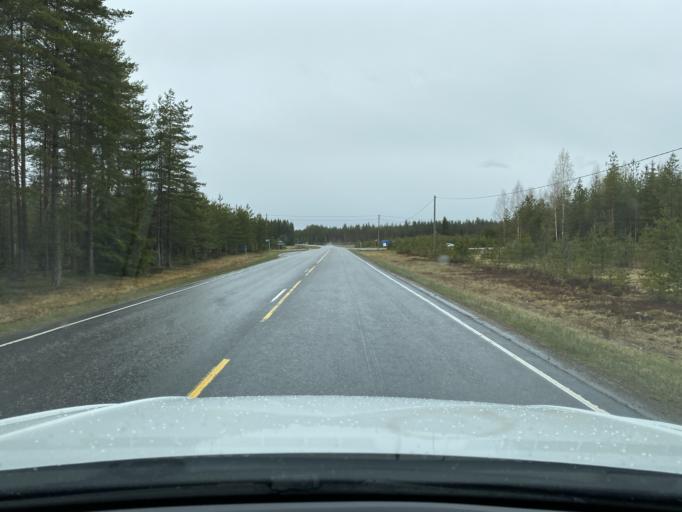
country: FI
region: Satakunta
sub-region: Pori
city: Vampula
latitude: 60.9544
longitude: 22.6675
